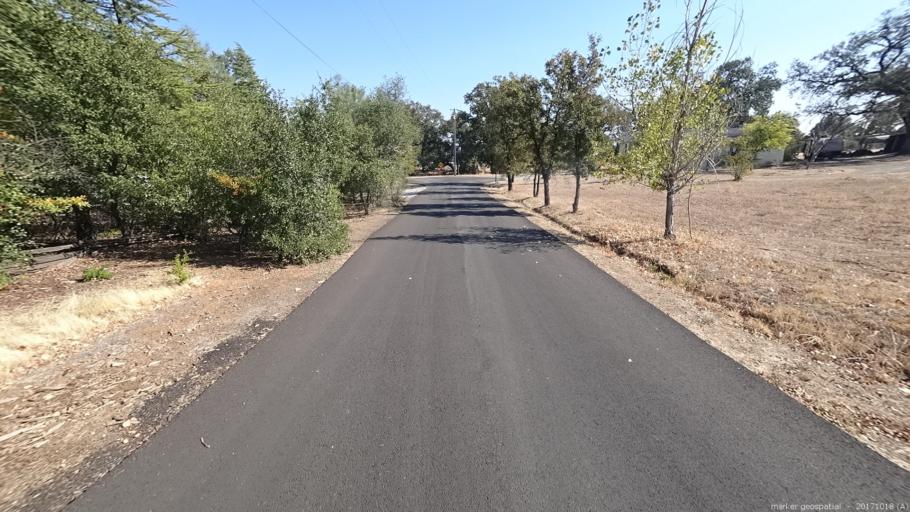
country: US
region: California
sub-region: Shasta County
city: Palo Cedro
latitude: 40.5426
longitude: -122.1791
